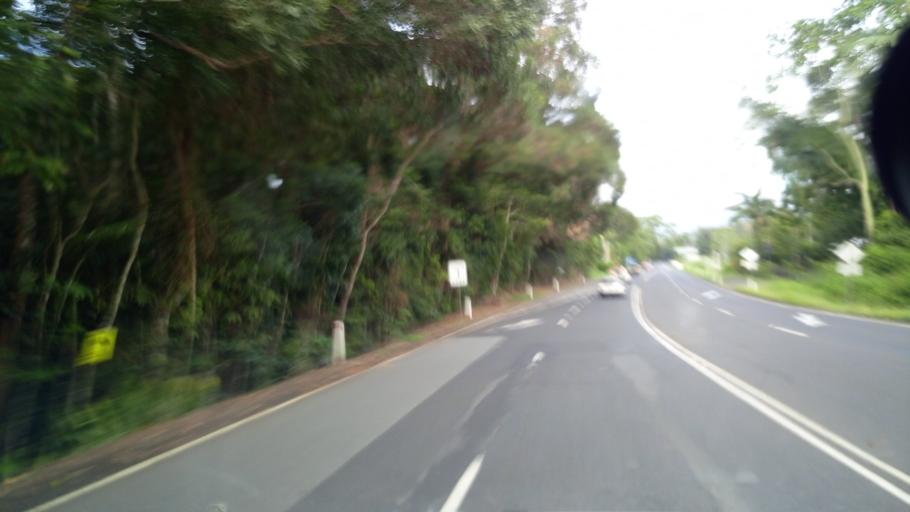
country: AU
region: Queensland
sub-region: Tablelands
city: Kuranda
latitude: -16.8181
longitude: 145.6453
